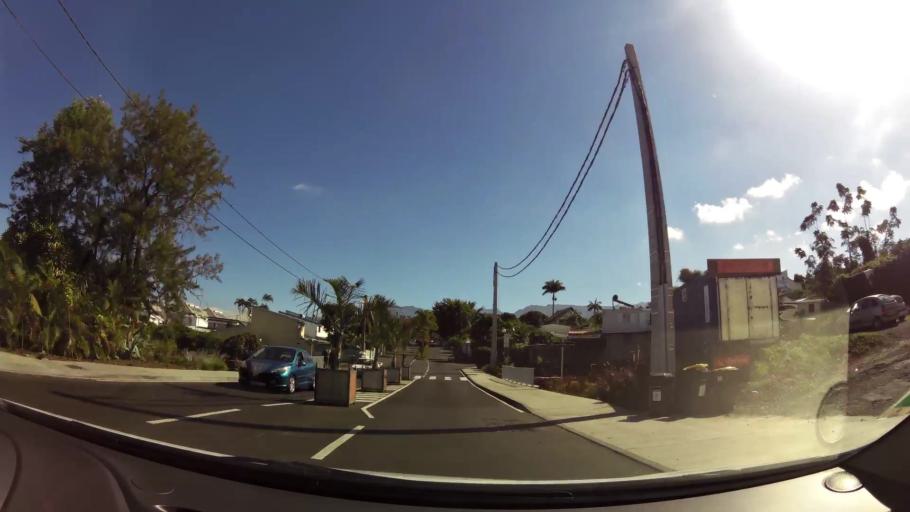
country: RE
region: Reunion
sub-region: Reunion
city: Le Tampon
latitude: -21.2710
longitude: 55.5150
